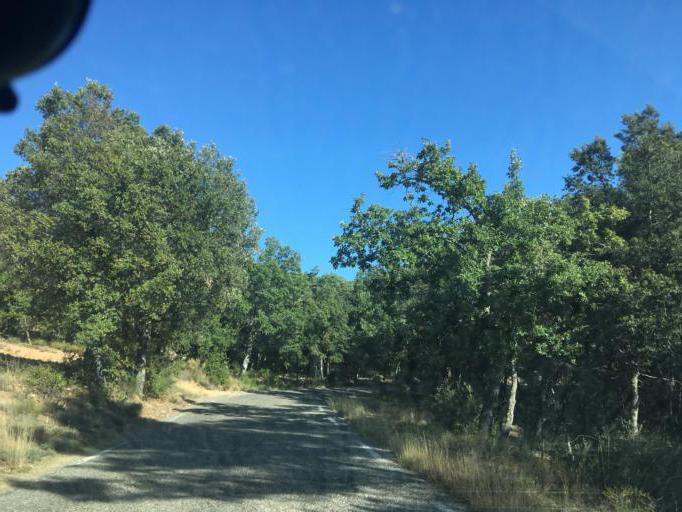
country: FR
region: Provence-Alpes-Cote d'Azur
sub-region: Departement du Var
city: Regusse
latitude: 43.7252
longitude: 6.1287
